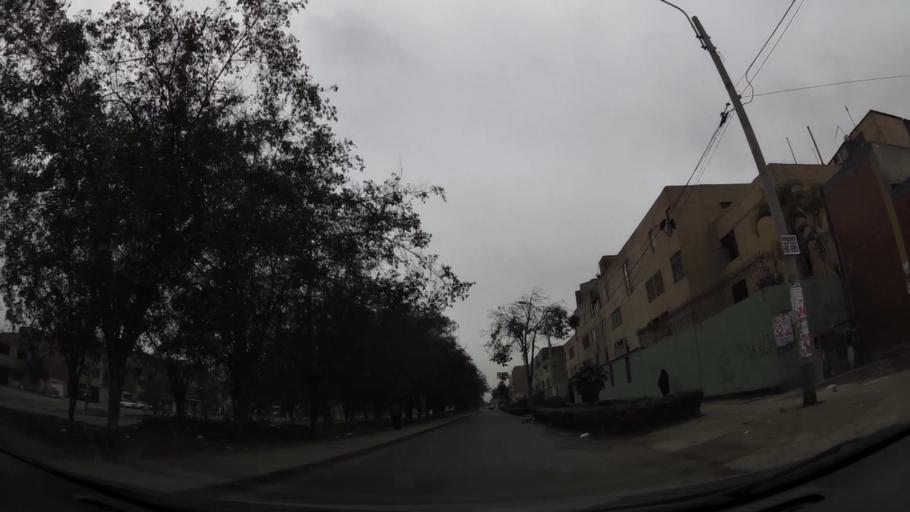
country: PE
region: Lima
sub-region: Lima
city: Independencia
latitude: -11.9674
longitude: -77.0611
